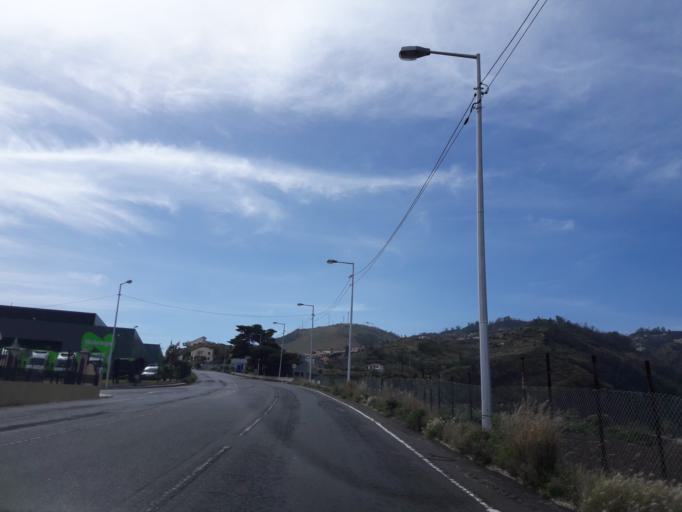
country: PT
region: Madeira
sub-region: Santa Cruz
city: Santa Cruz
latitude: 32.6602
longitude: -16.8136
